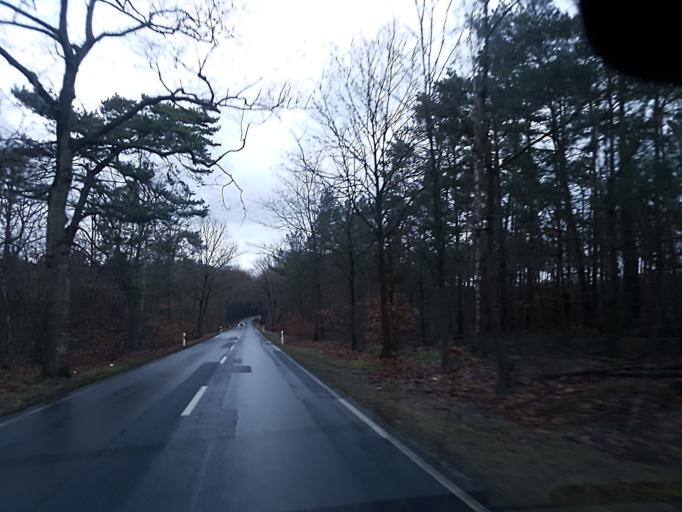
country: DE
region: Brandenburg
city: Hohenleipisch
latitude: 51.5088
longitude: 13.5624
